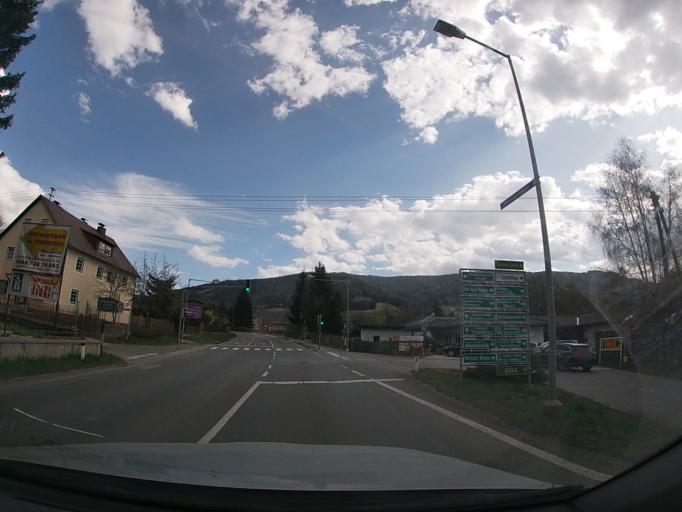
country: AT
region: Styria
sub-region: Politischer Bezirk Murau
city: Sankt Lorenzen bei Scheifling
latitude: 47.1508
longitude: 14.4121
